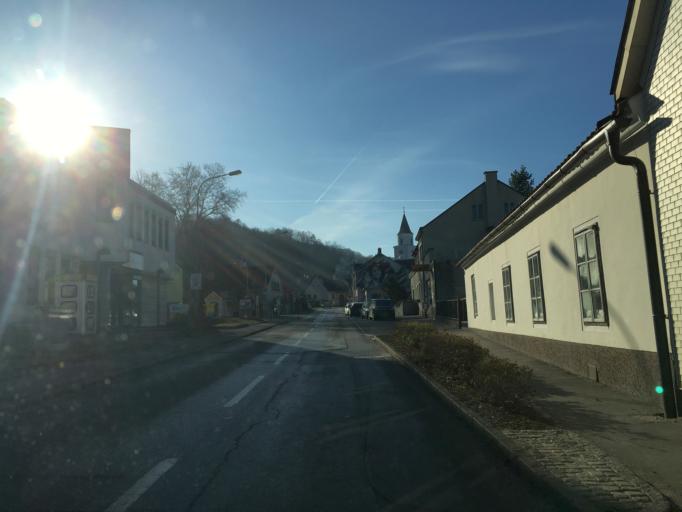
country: AT
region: Lower Austria
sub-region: Politischer Bezirk Tulln
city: Wordern
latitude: 48.3226
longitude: 16.2096
